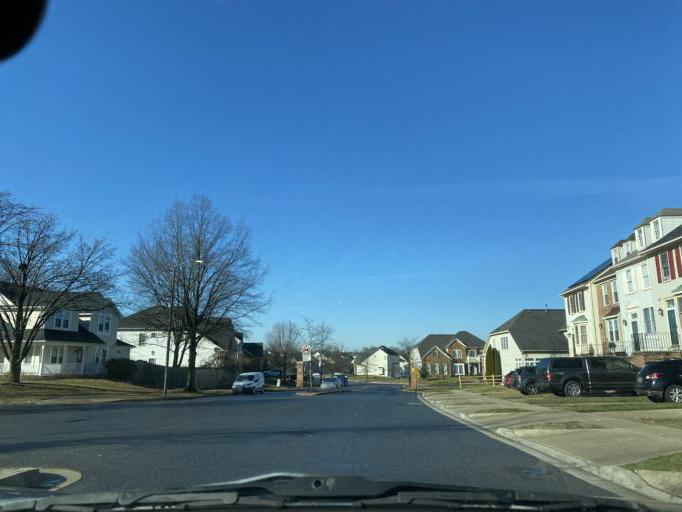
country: US
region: Maryland
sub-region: Prince George's County
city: South Laurel
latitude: 39.0844
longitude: -76.8705
